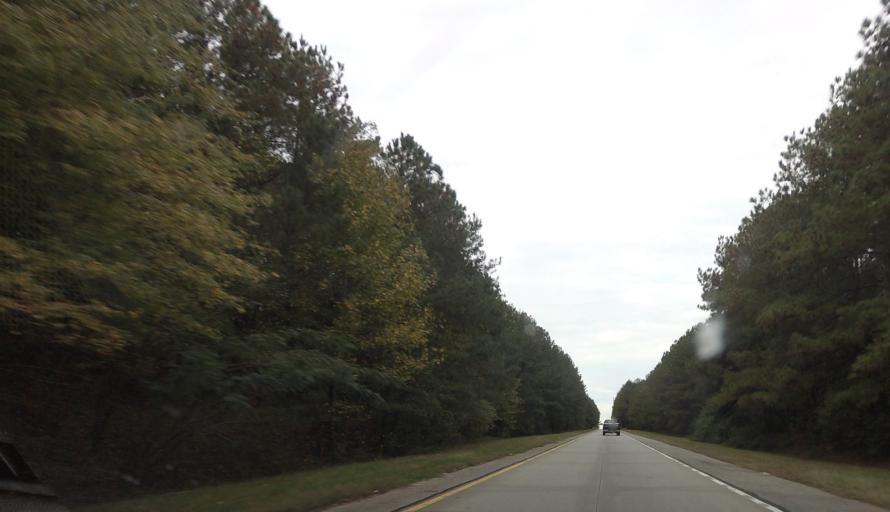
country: US
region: Alabama
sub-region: Russell County
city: Phenix City
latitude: 32.5540
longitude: -84.9276
